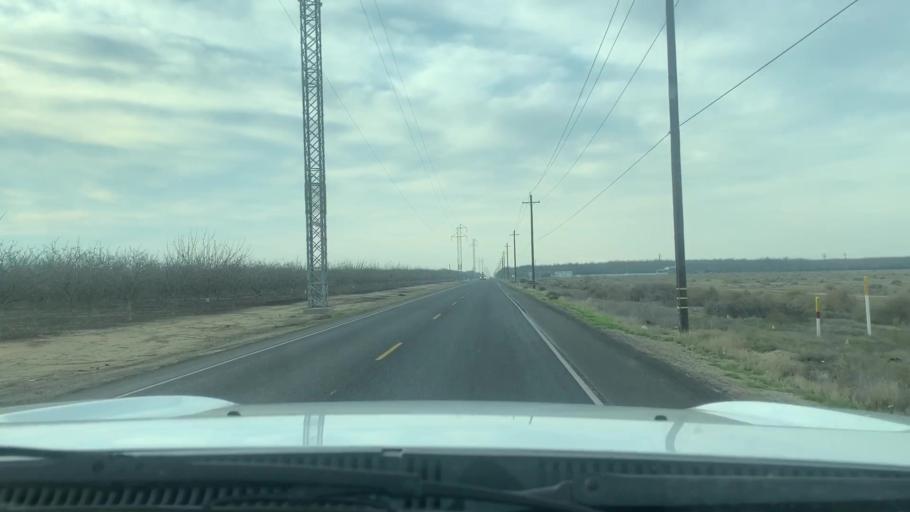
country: US
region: California
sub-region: Kern County
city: Shafter
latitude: 35.4418
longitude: -119.2919
